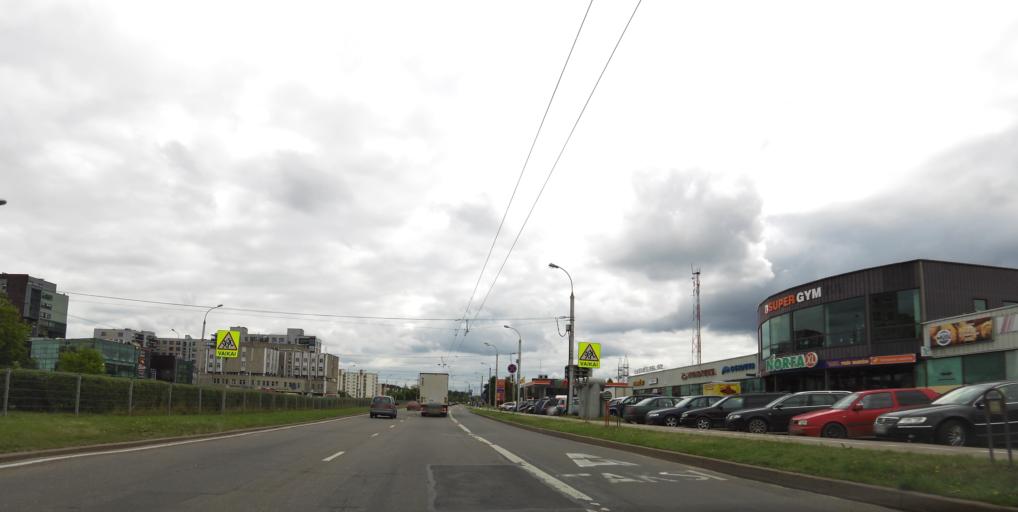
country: LT
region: Vilnius County
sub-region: Vilnius
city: Fabijoniskes
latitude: 54.7245
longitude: 25.2337
